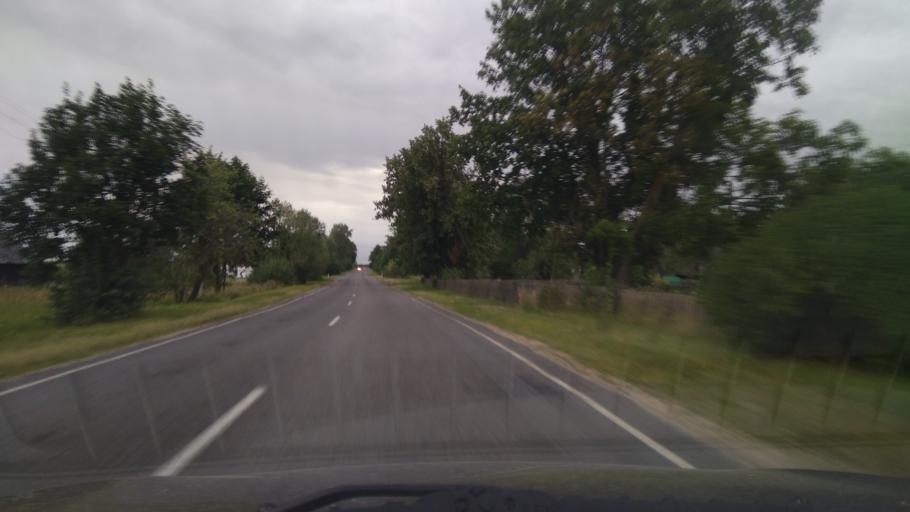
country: BY
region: Brest
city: Byaroza
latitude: 52.4233
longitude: 24.9812
